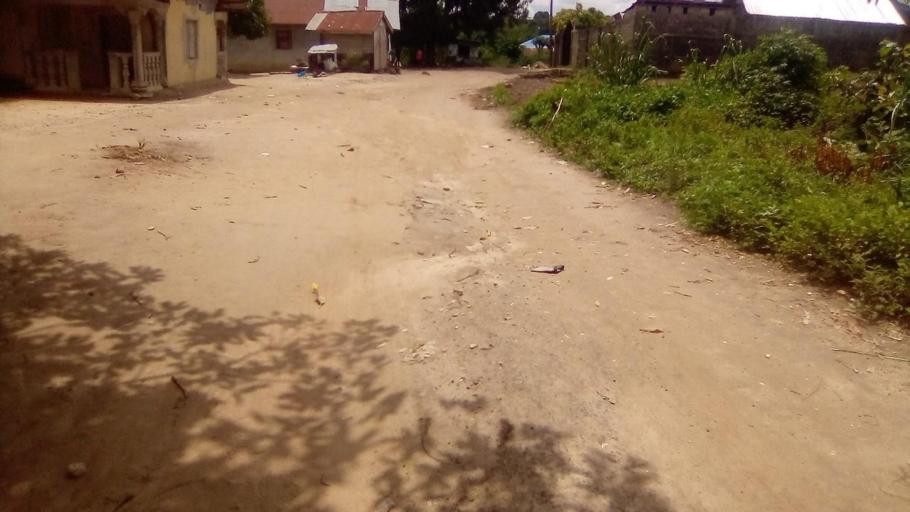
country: SL
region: Southern Province
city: Bo
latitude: 7.9380
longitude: -11.7472
